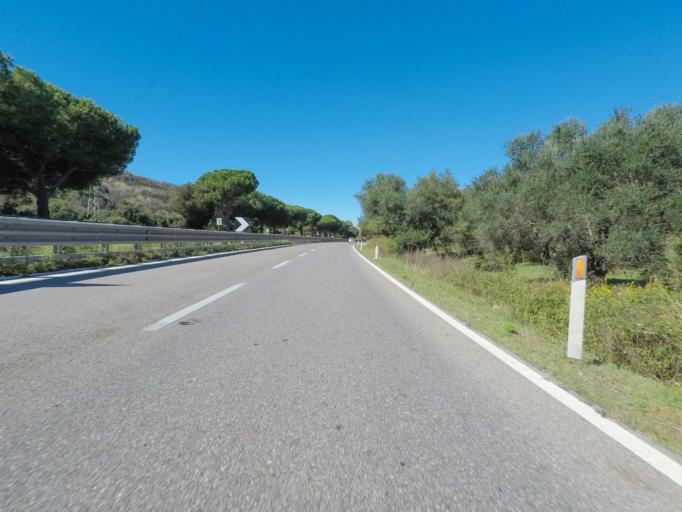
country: IT
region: Tuscany
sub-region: Provincia di Grosseto
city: Orbetello Scalo
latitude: 42.4218
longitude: 11.2895
